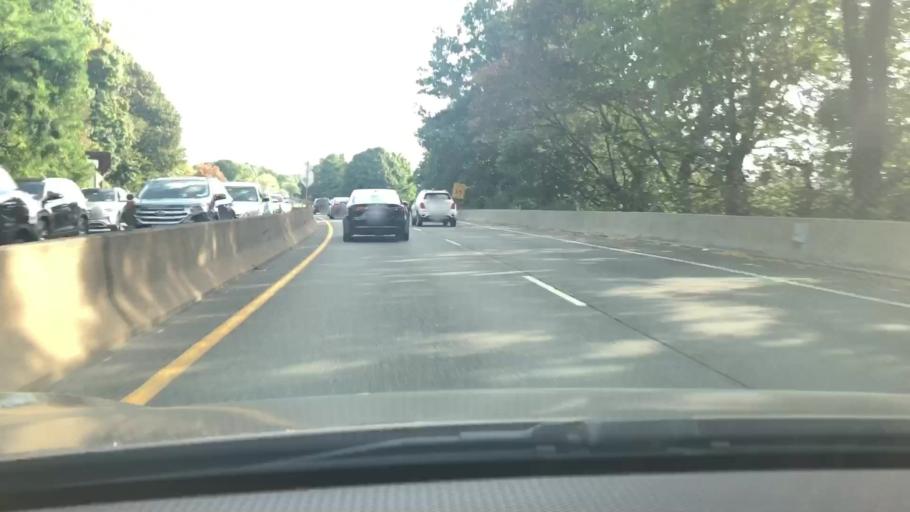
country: US
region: New York
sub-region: Westchester County
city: Pelham Manor
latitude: 40.8945
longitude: -73.8169
